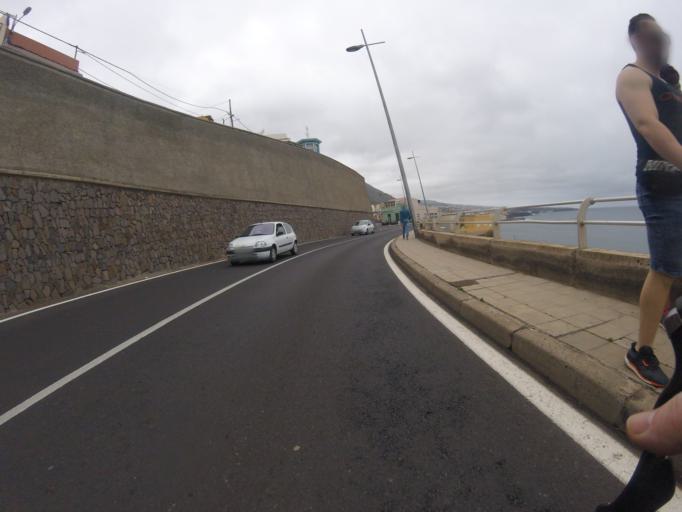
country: ES
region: Canary Islands
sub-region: Provincia de Santa Cruz de Tenerife
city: Tegueste
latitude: 28.5634
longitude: -16.3315
